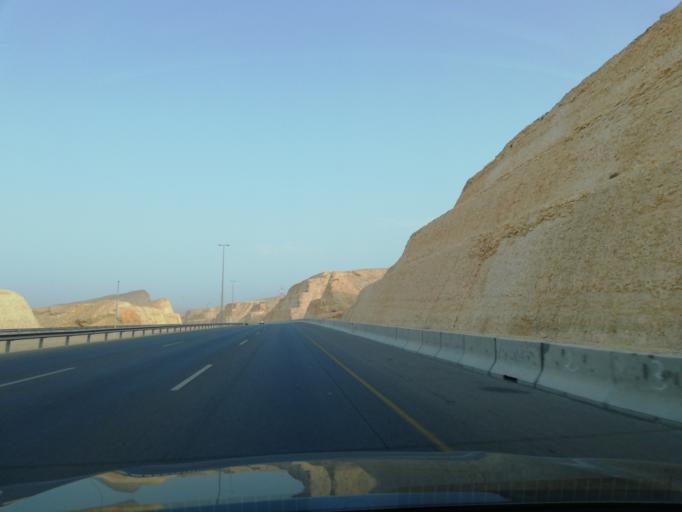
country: OM
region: Muhafazat Masqat
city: As Sib al Jadidah
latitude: 23.5476
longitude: 58.2376
